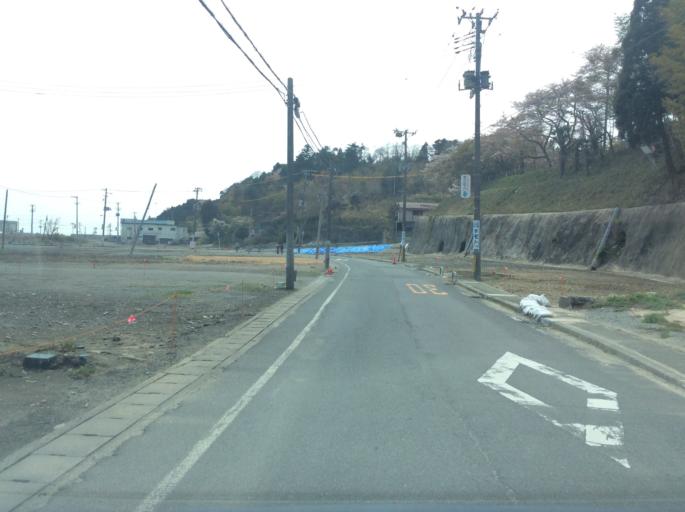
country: JP
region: Fukushima
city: Namie
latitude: 37.3353
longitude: 141.0211
